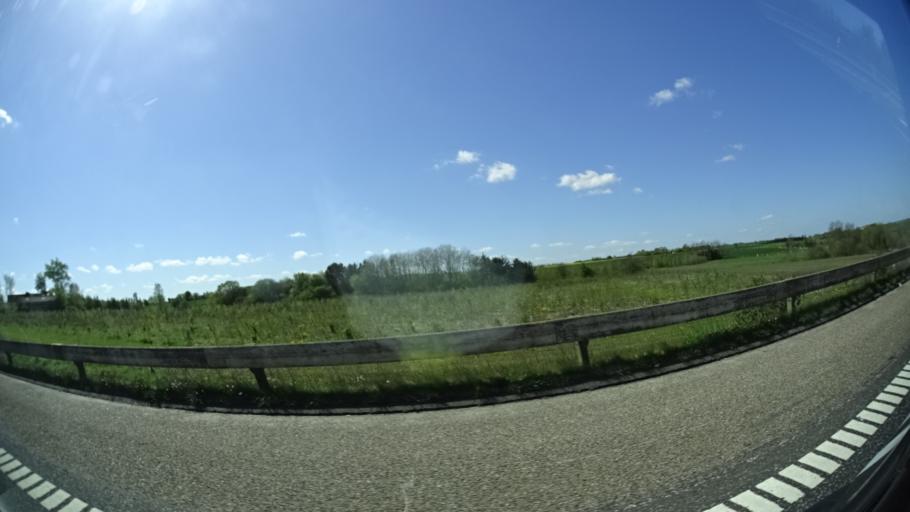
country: DK
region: Central Jutland
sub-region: Favrskov Kommune
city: Hadsten
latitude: 56.3425
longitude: 10.1207
